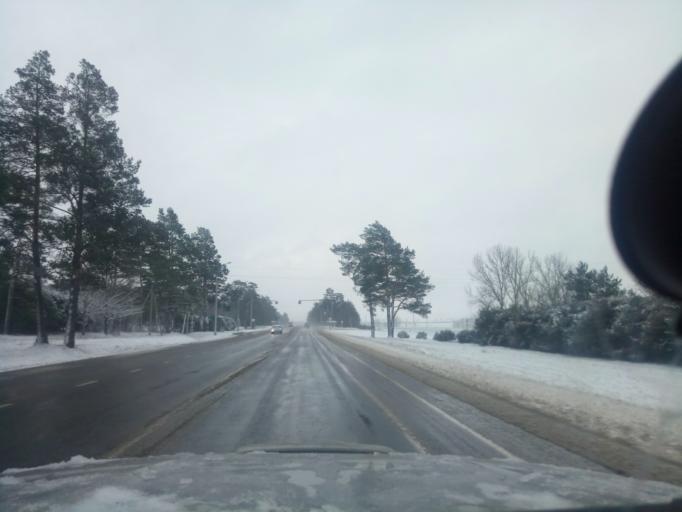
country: BY
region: Minsk
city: Nyasvizh
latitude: 53.2478
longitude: 26.6240
